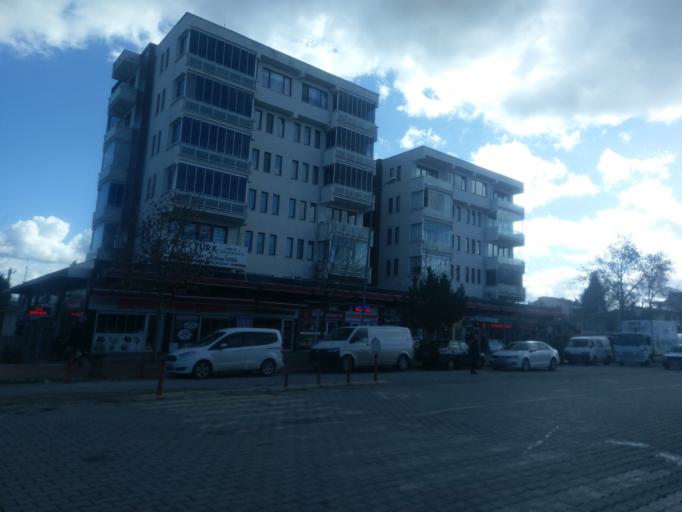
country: TR
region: Kuetahya
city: Gediz
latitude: 38.9908
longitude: 29.3956
